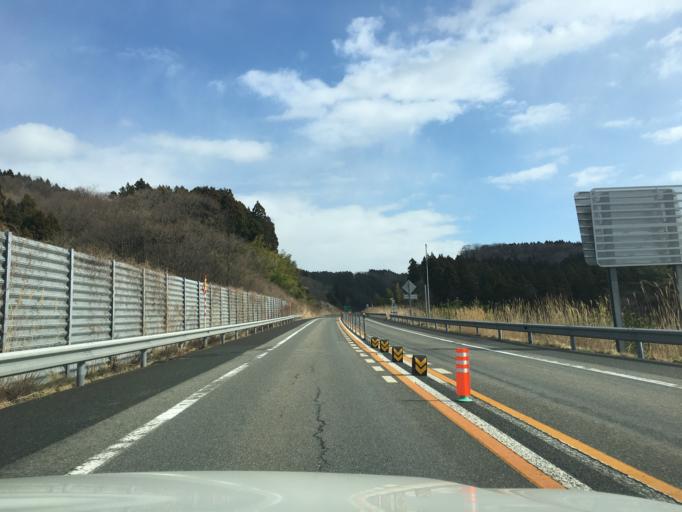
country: JP
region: Akita
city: Akita Shi
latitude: 39.5519
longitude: 140.0769
